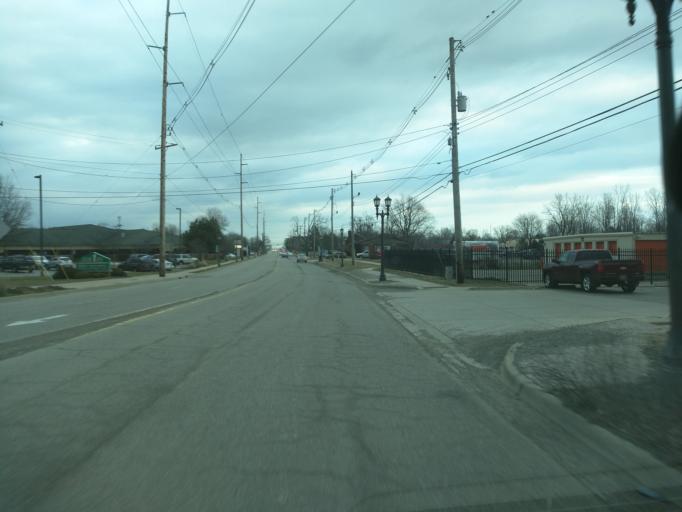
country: US
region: Michigan
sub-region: Ingham County
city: Lansing
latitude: 42.7607
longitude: -84.5294
